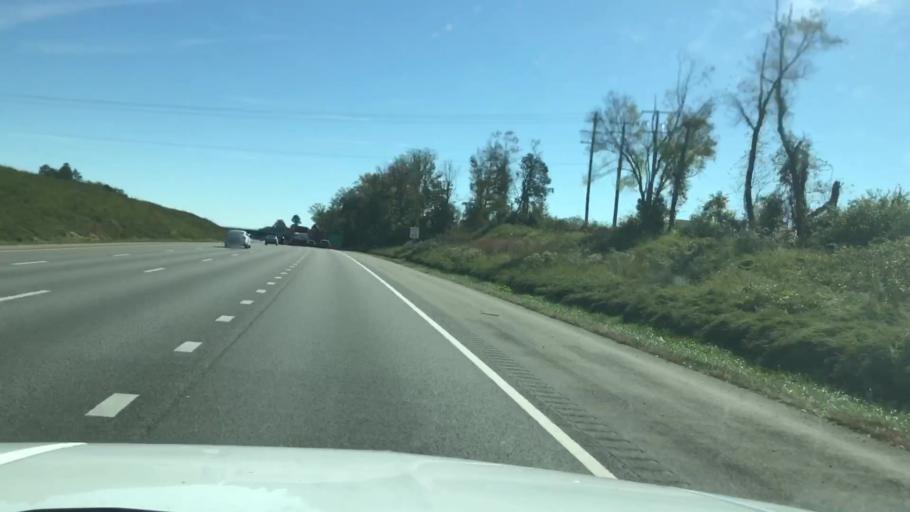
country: US
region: Virginia
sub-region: Henrico County
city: Short Pump
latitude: 37.6649
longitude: -77.6367
